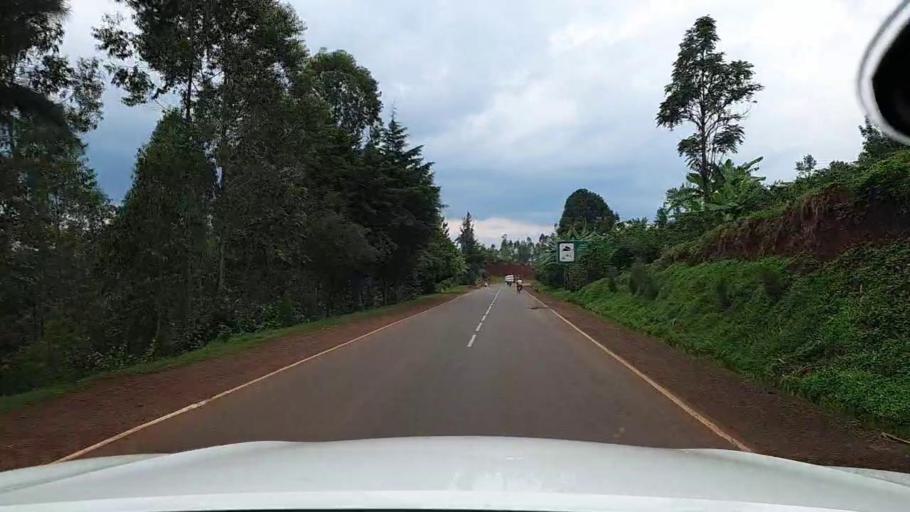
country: RW
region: Western Province
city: Cyangugu
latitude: -2.6457
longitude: 28.9611
